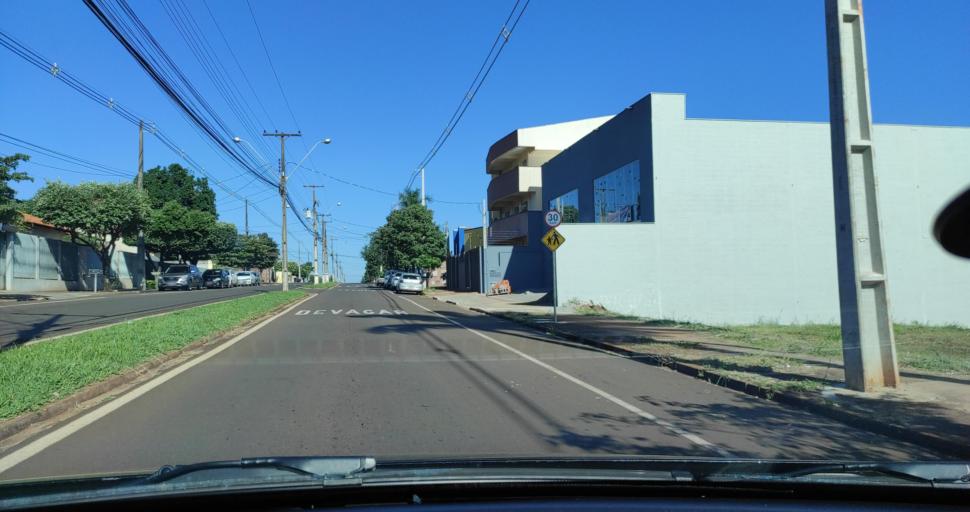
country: BR
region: Parana
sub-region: Ibipora
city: Ibipora
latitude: -23.2712
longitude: -51.0606
